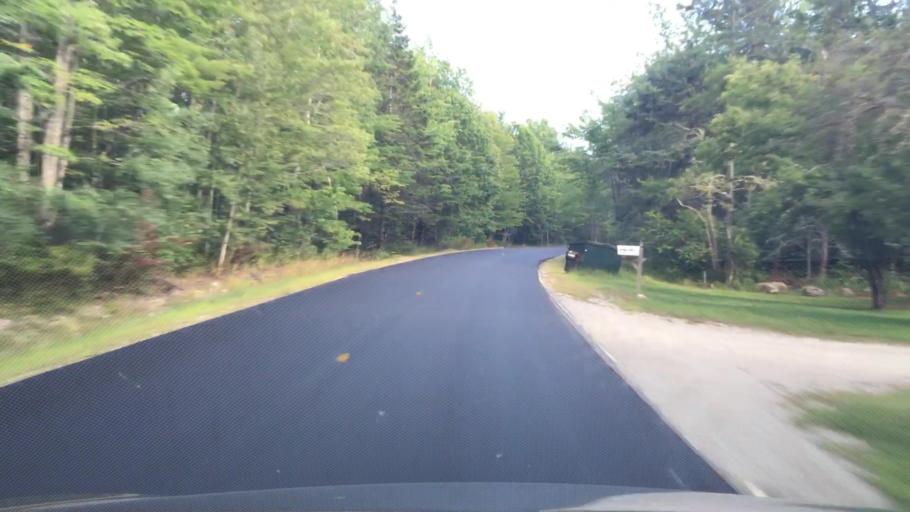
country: US
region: Maine
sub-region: Hancock County
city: Orland
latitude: 44.5441
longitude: -68.6181
